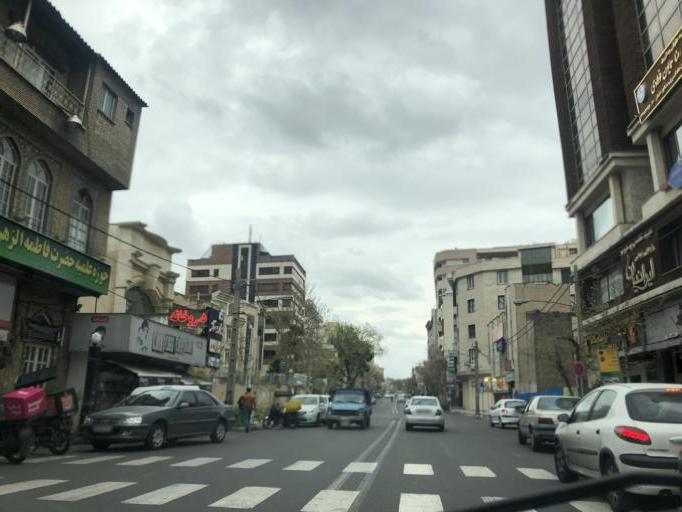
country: IR
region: Tehran
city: Tajrish
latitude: 35.7803
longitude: 51.4608
